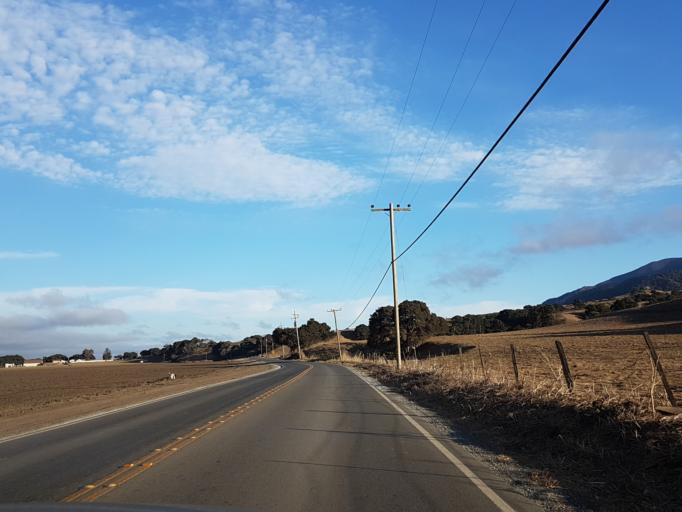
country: US
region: California
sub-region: Monterey County
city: Chualar
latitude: 36.5777
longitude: -121.5905
